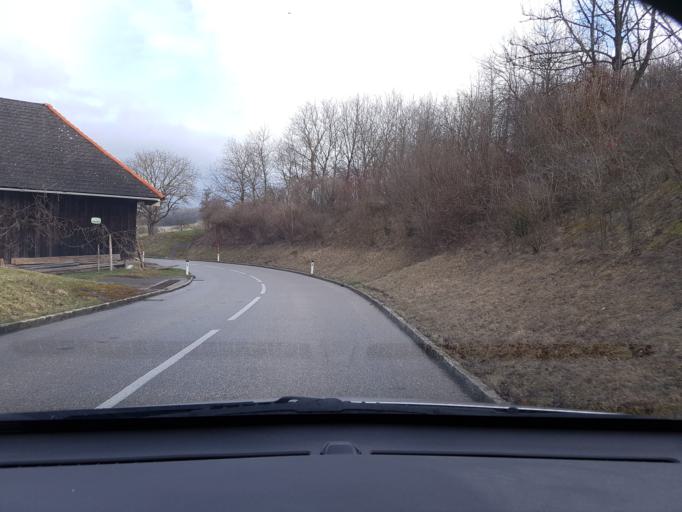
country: AT
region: Upper Austria
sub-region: Politischer Bezirk Linz-Land
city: Sankt Florian
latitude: 48.1824
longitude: 14.3792
